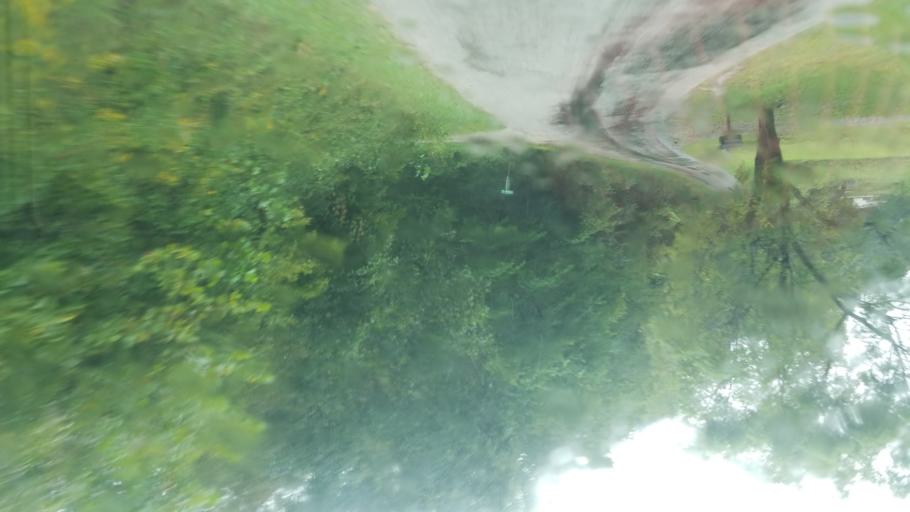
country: US
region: Kentucky
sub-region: Lewis County
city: Vanceburg
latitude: 38.7937
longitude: -83.2560
